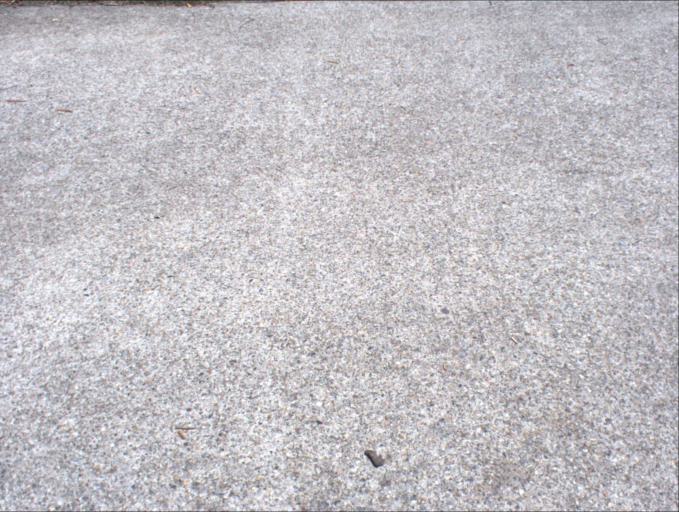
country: AU
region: Queensland
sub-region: Logan
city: Beenleigh
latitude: -27.6907
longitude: 153.2153
